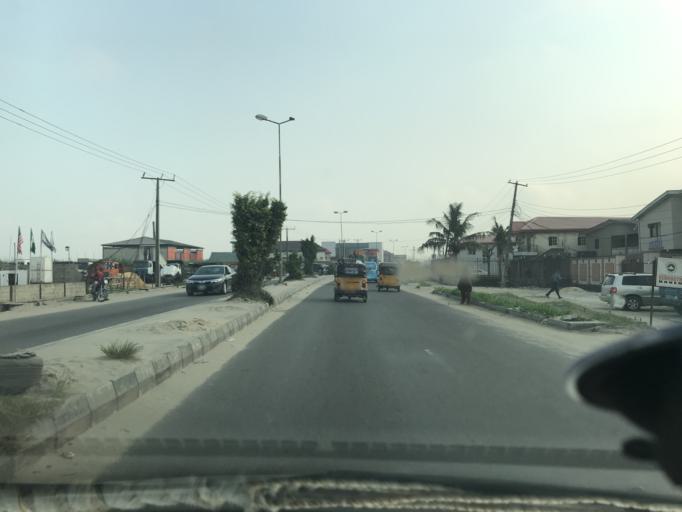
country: NG
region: Lagos
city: Ikoyi
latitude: 6.4846
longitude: 3.5747
